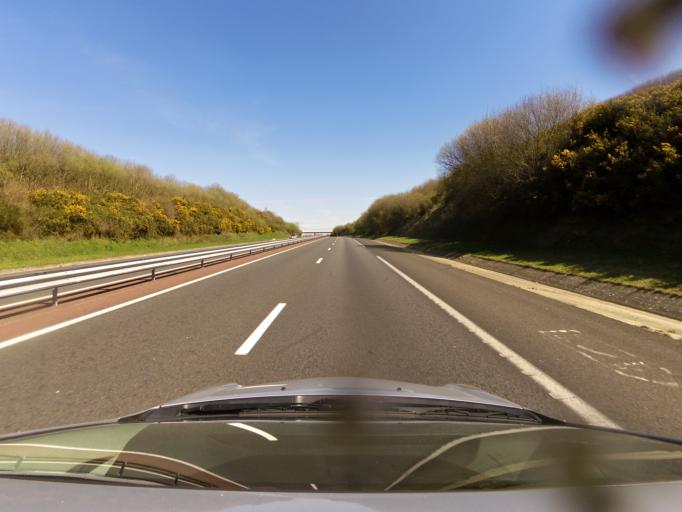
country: FR
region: Lower Normandy
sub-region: Departement de la Manche
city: Villedieu-les-Poeles
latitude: 48.8244
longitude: -1.2470
